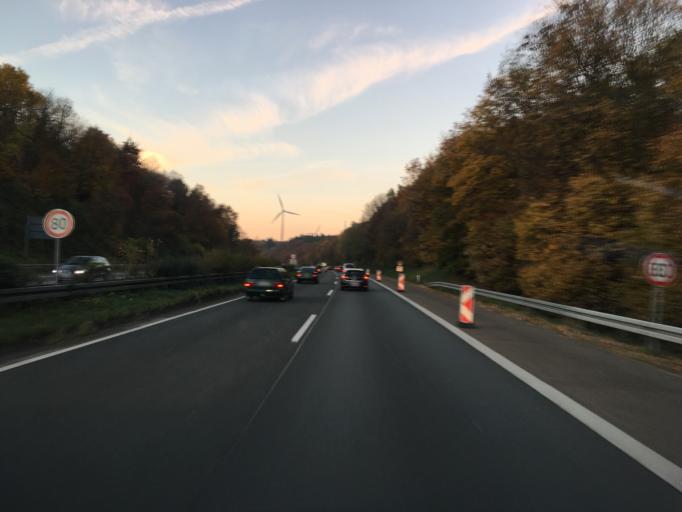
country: DE
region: North Rhine-Westphalia
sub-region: Regierungsbezirk Arnsberg
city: Nachrodt-Wiblingwerde
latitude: 51.3071
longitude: 7.5553
